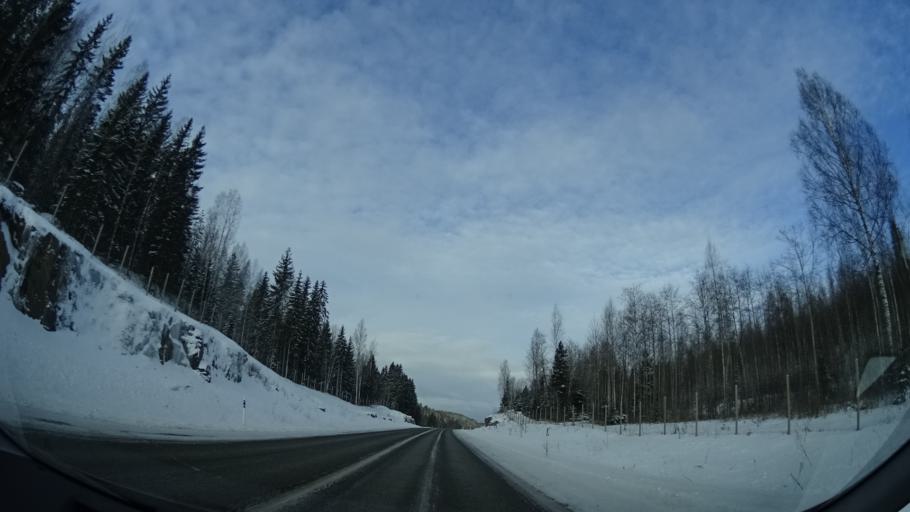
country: FI
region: Uusimaa
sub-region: Helsinki
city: Karkkila
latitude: 60.5757
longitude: 24.1434
